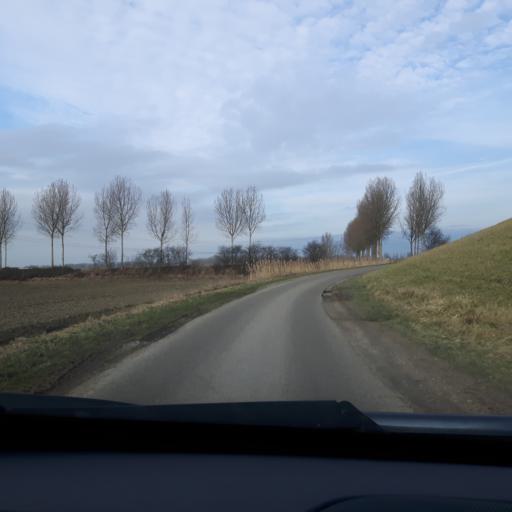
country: NL
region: Zeeland
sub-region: Gemeente Goes
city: Goes
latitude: 51.4435
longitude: 3.9206
